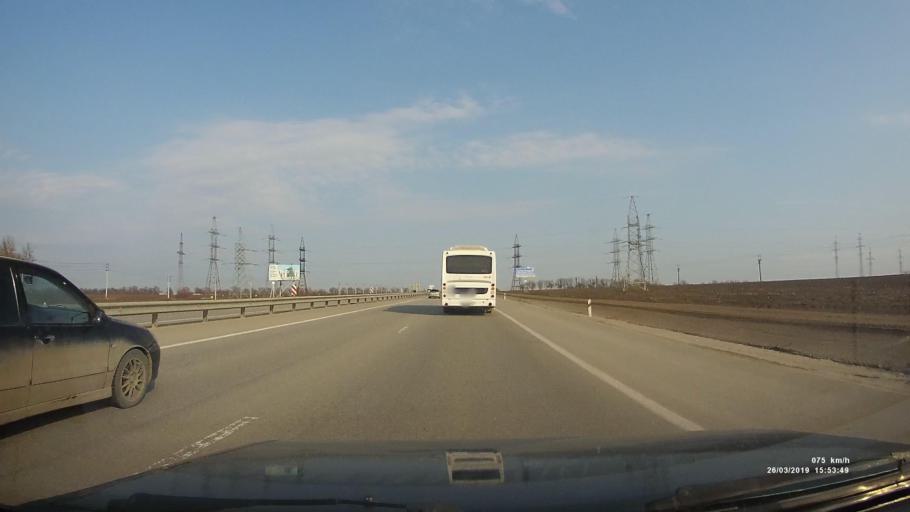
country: RU
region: Rostov
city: Krym
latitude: 47.2716
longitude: 39.5471
